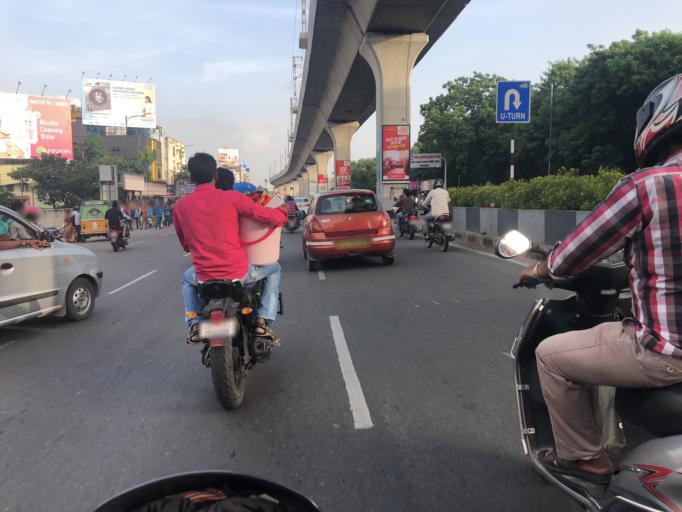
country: IN
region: Telangana
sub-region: Rangareddi
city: Kukatpalli
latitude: 17.4467
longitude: 78.4388
